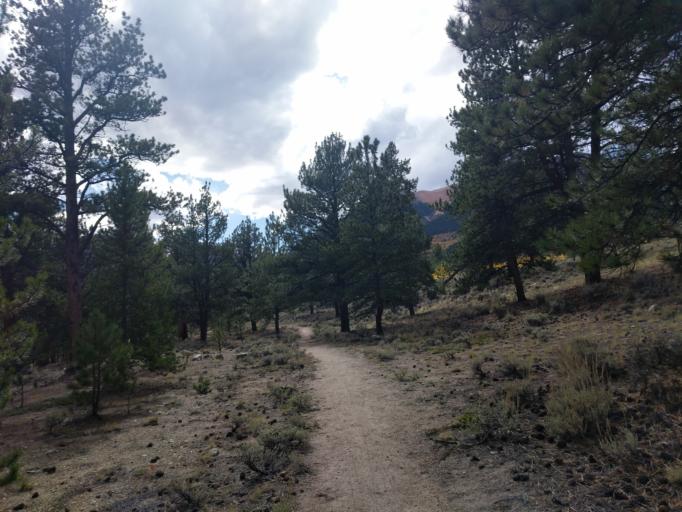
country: US
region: Colorado
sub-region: Lake County
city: Leadville
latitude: 39.0980
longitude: -106.3693
